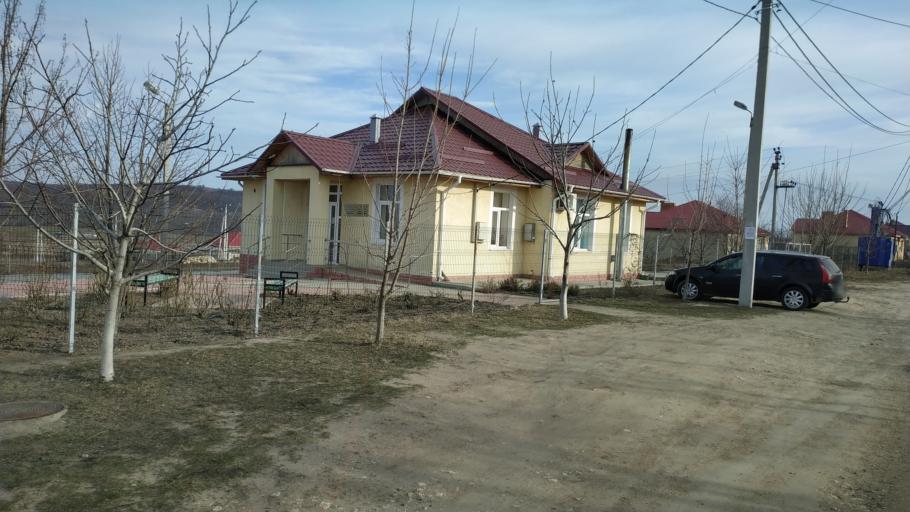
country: RO
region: Vaslui
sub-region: Comuna Dranceni
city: Dranceni
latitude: 46.8387
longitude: 28.1836
